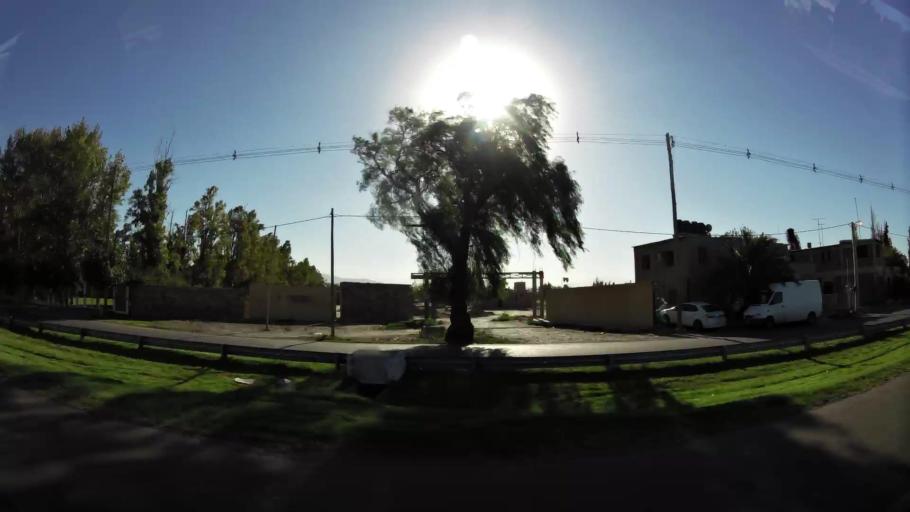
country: AR
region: San Juan
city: Villa Krause
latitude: -31.5682
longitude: -68.5169
